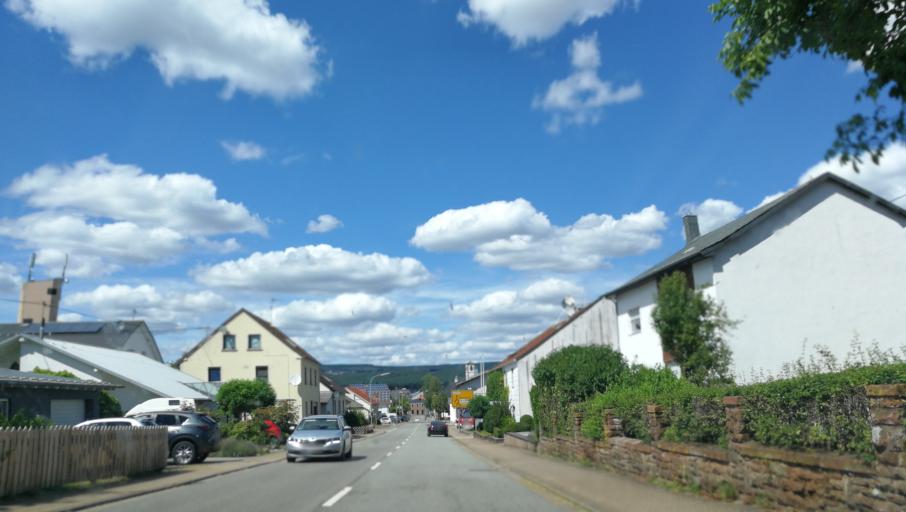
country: DE
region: Saarland
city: Losheim
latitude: 49.5042
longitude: 6.7447
